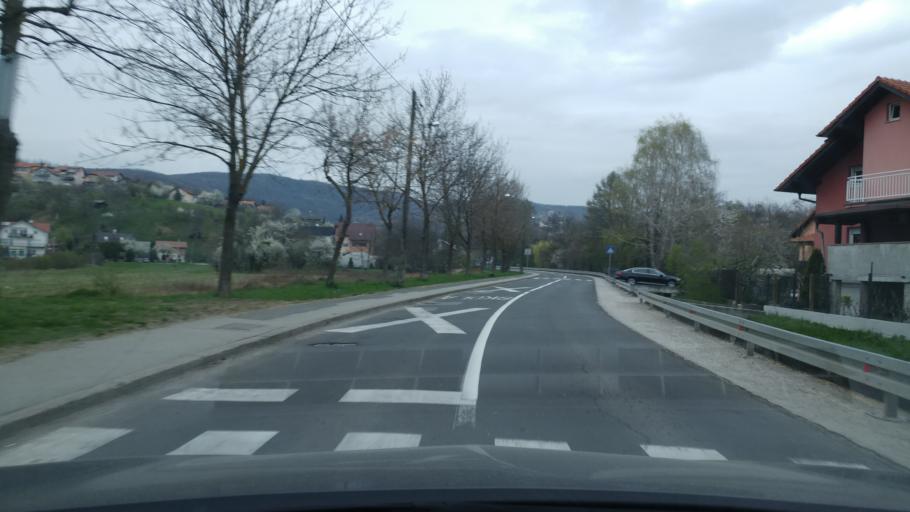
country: HR
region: Grad Zagreb
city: Stenjevec
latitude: 45.8166
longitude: 15.8693
